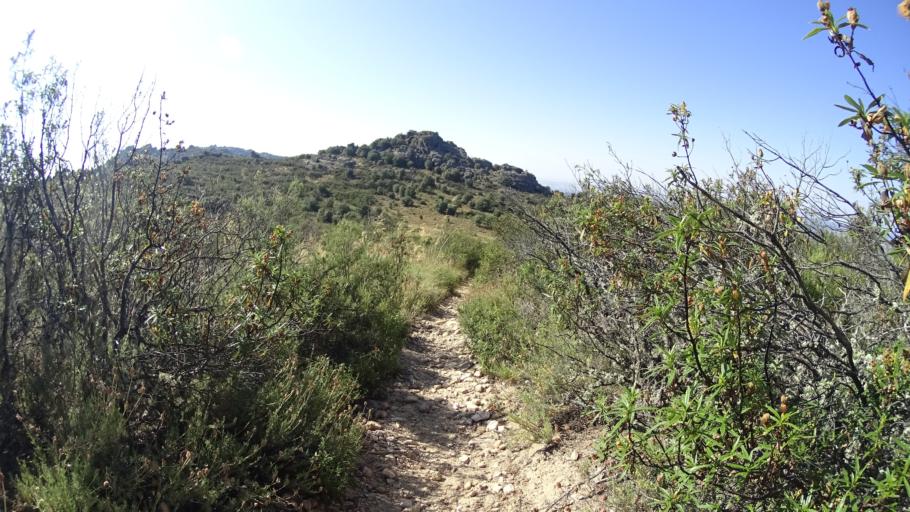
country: ES
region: Madrid
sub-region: Provincia de Madrid
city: Hoyo de Manzanares
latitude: 40.6485
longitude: -3.9386
